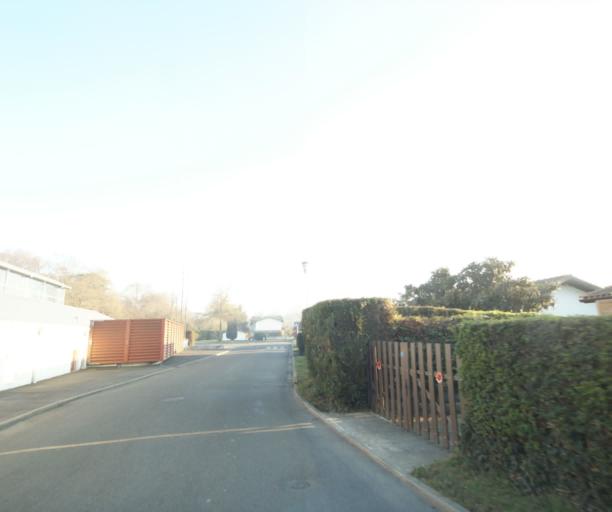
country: FR
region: Aquitaine
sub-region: Departement des Pyrenees-Atlantiques
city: Urrugne
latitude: 43.3650
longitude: -1.6944
